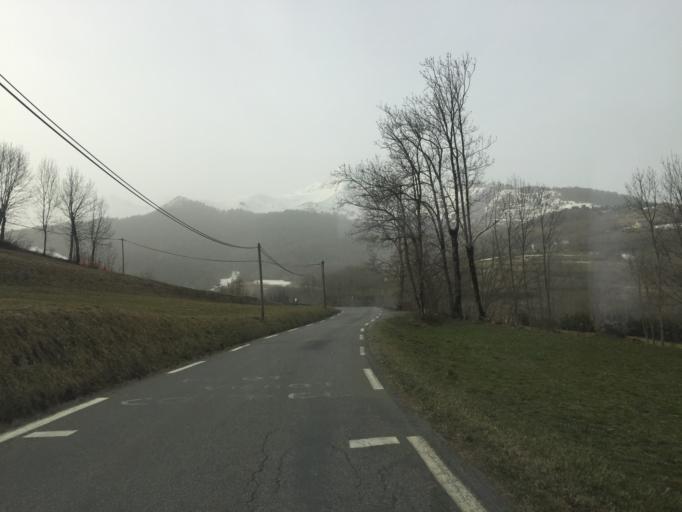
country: FR
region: Midi-Pyrenees
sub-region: Departement des Hautes-Pyrenees
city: Saint-Lary-Soulan
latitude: 42.8119
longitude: 0.3478
